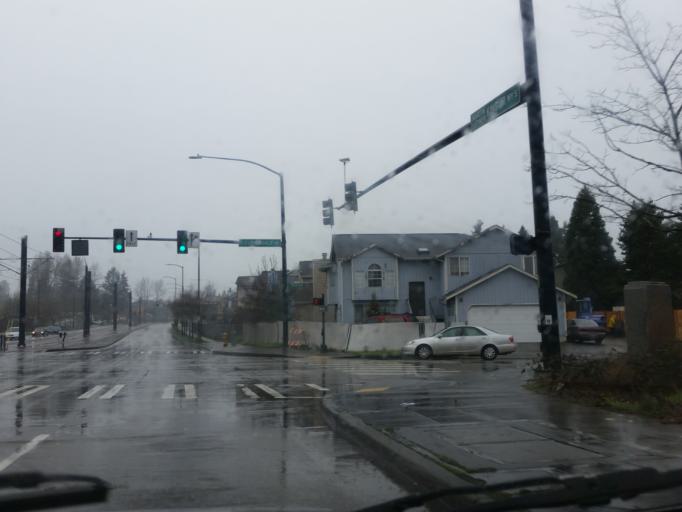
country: US
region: Washington
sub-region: King County
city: Riverton
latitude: 47.5259
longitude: -122.2789
